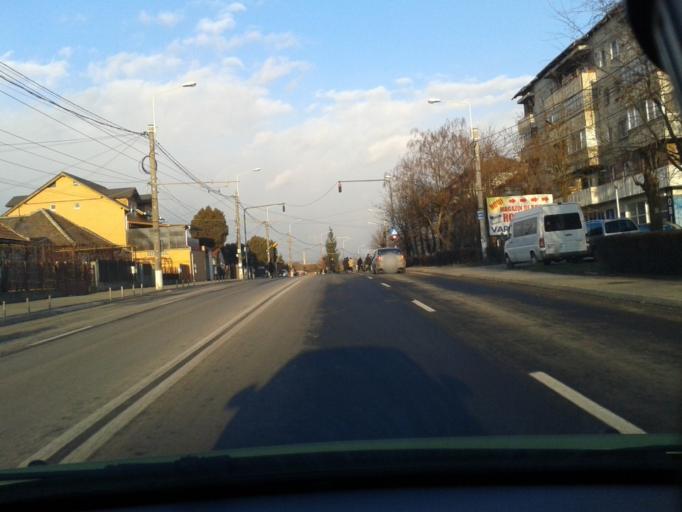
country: RO
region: Sibiu
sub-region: Municipiul Medias
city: Medias
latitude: 46.1498
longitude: 24.3287
